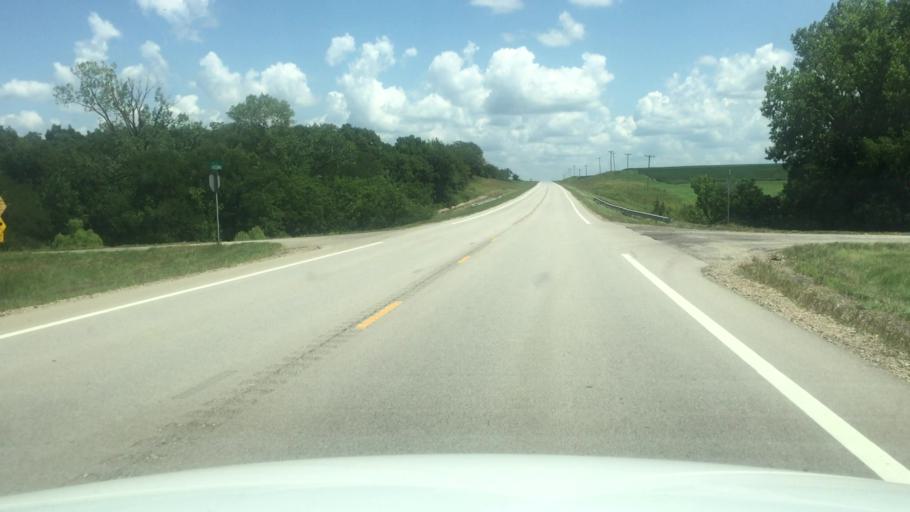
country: US
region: Kansas
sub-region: Brown County
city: Horton
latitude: 39.6673
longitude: -95.4524
